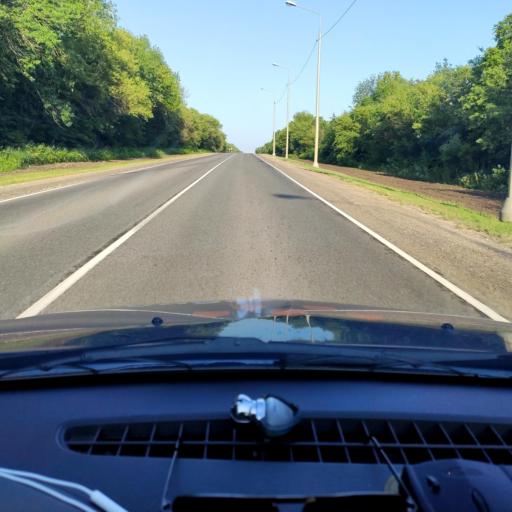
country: RU
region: Orjol
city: Livny
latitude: 52.4269
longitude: 37.7670
